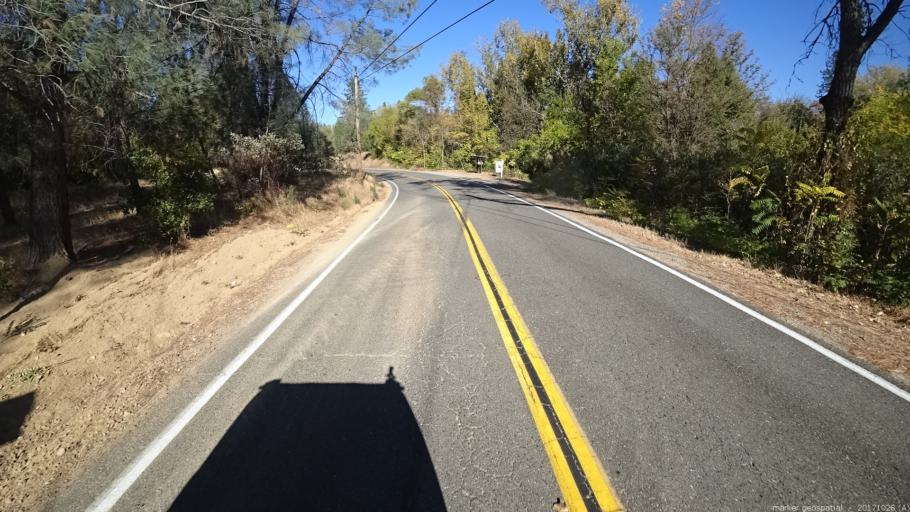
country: US
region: California
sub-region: Shasta County
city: Shasta
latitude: 40.6233
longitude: -122.4662
